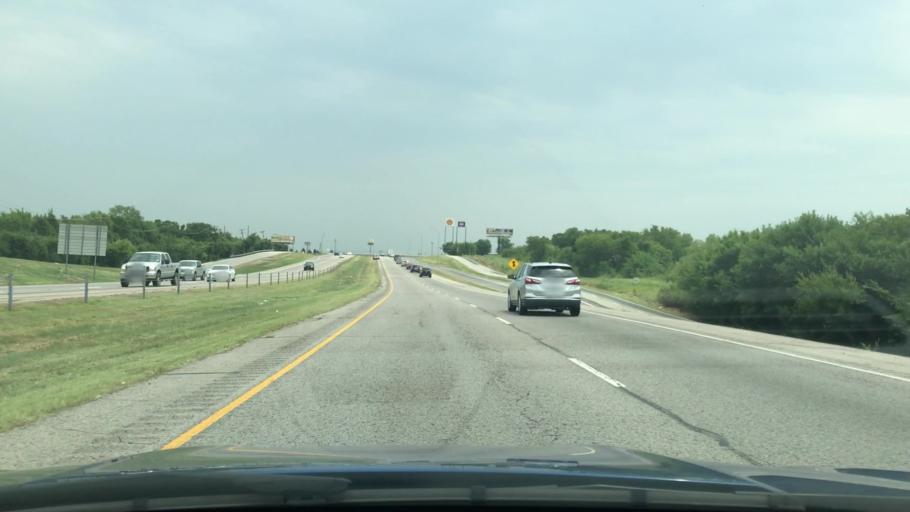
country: US
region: Texas
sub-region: Kaufman County
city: Forney
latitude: 32.7585
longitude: -96.4753
